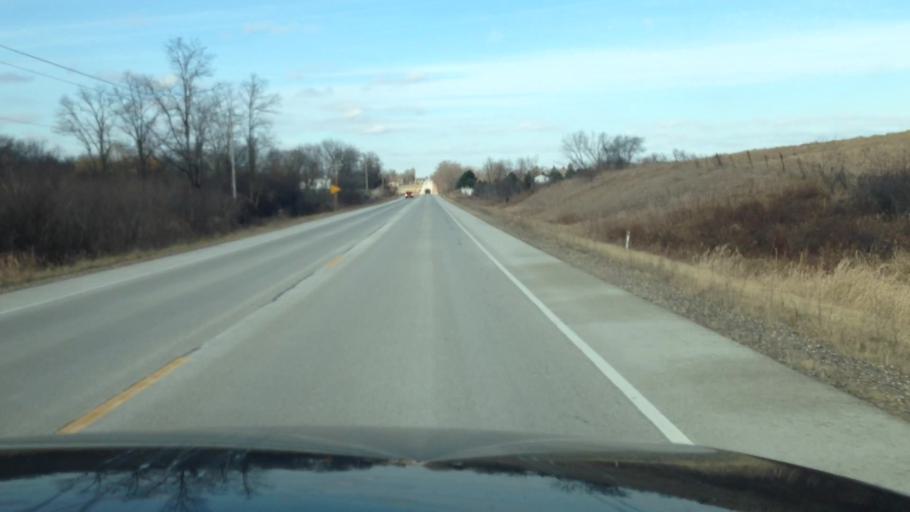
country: US
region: Wisconsin
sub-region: Walworth County
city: East Troy
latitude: 42.7033
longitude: -88.4050
